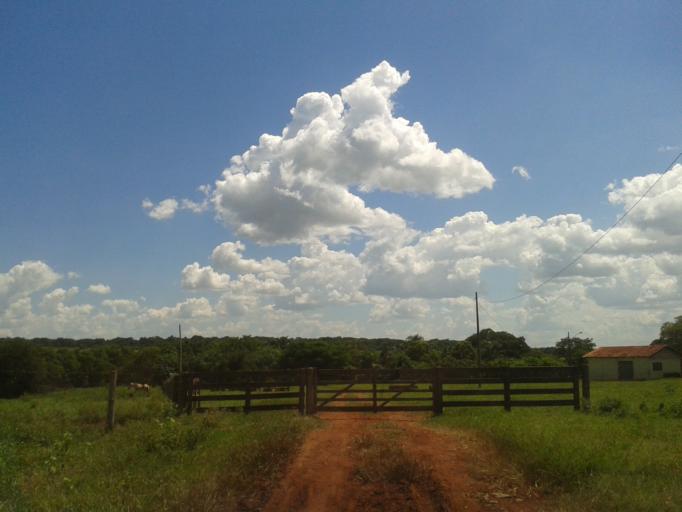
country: BR
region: Minas Gerais
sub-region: Santa Vitoria
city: Santa Vitoria
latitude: -19.1081
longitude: -50.5224
